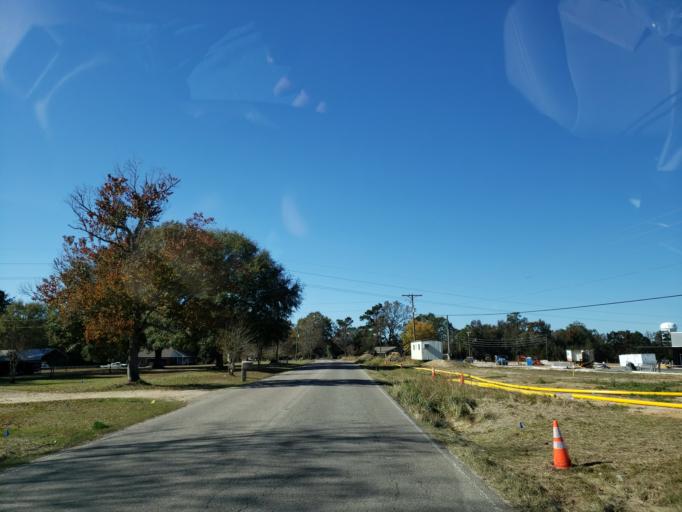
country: US
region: Mississippi
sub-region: Lamar County
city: West Hattiesburg
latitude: 31.3096
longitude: -89.3956
